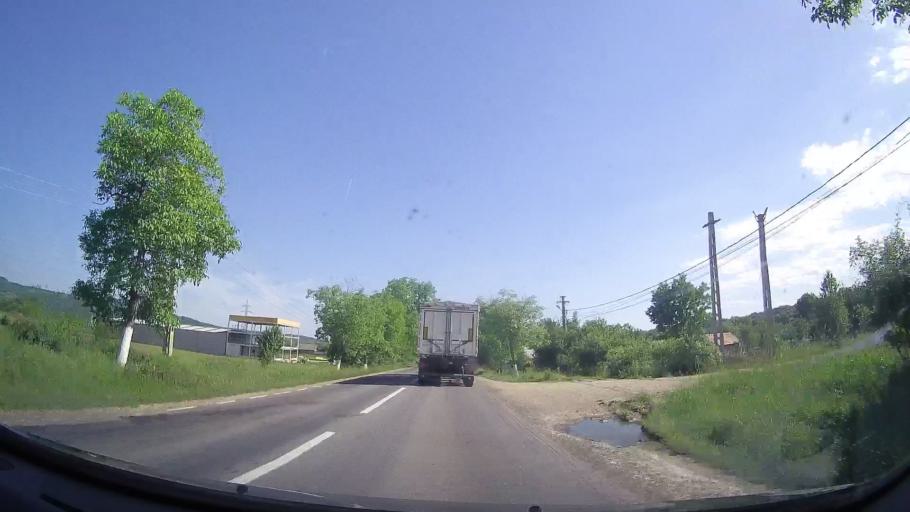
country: RO
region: Prahova
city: Drajna de Jos
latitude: 45.2375
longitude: 26.0286
